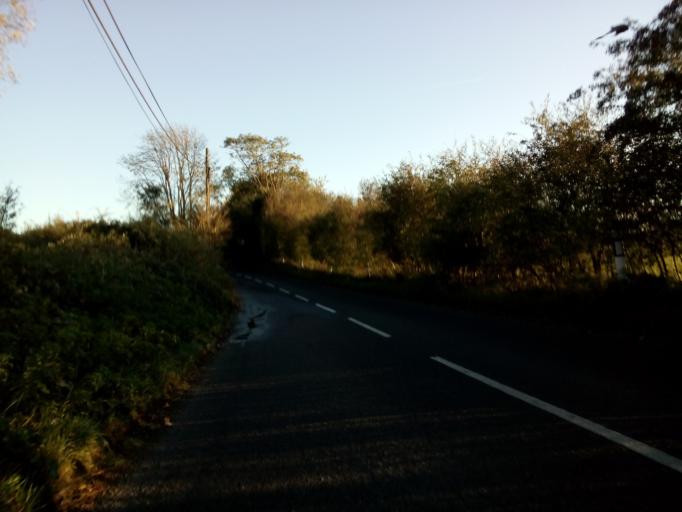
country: GB
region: England
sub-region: Suffolk
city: Sudbury
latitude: 51.9919
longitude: 0.7684
